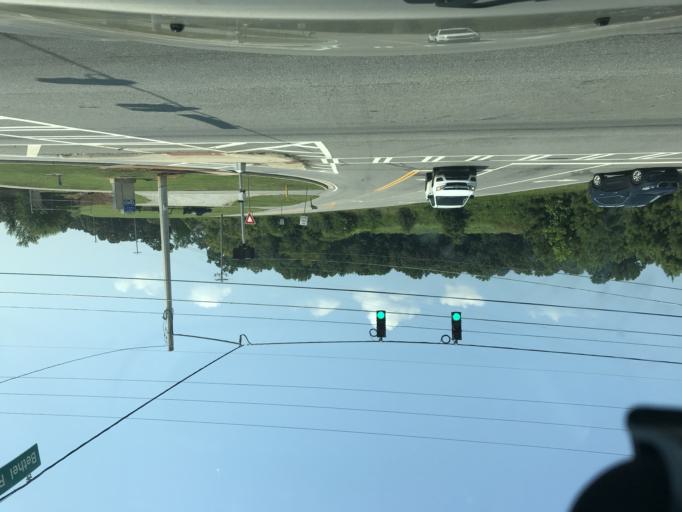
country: US
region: Georgia
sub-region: Hall County
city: Flowery Branch
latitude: 34.2513
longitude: -83.9976
